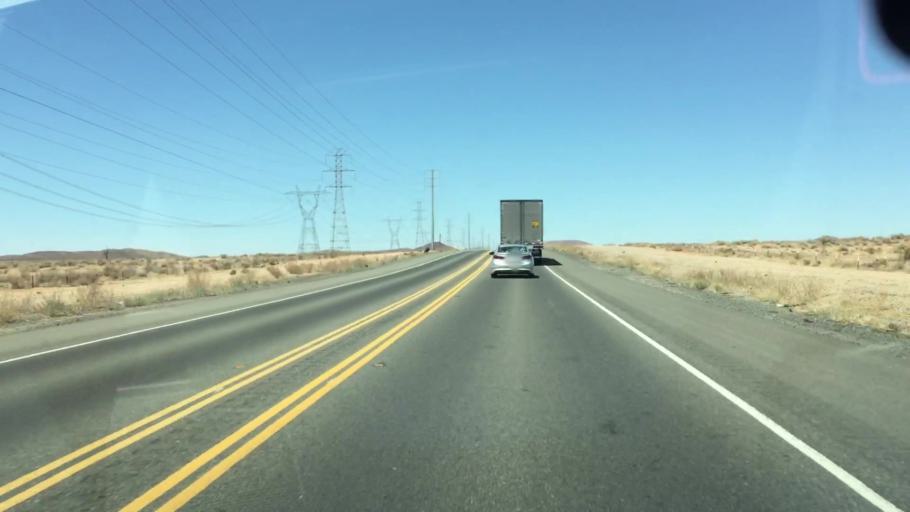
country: US
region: California
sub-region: Kern County
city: Boron
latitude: 34.8167
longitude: -117.4929
